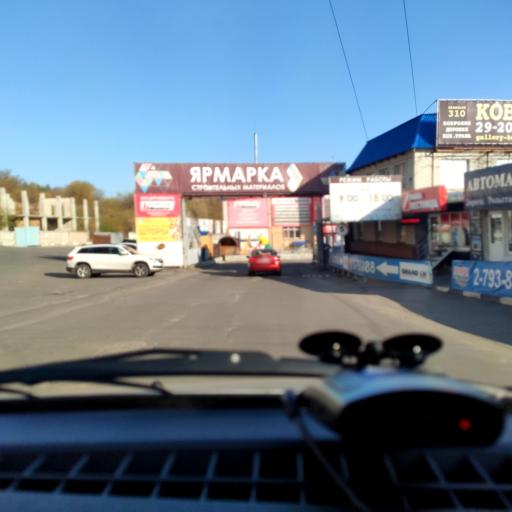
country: RU
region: Voronezj
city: Pridonskoy
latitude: 51.6720
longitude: 39.1234
